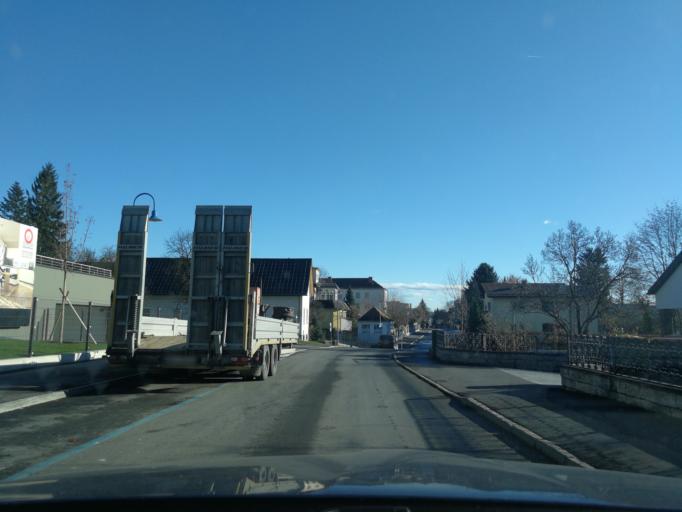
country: AT
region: Styria
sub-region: Politischer Bezirk Weiz
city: Gleisdorf
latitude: 47.1072
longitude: 15.7121
